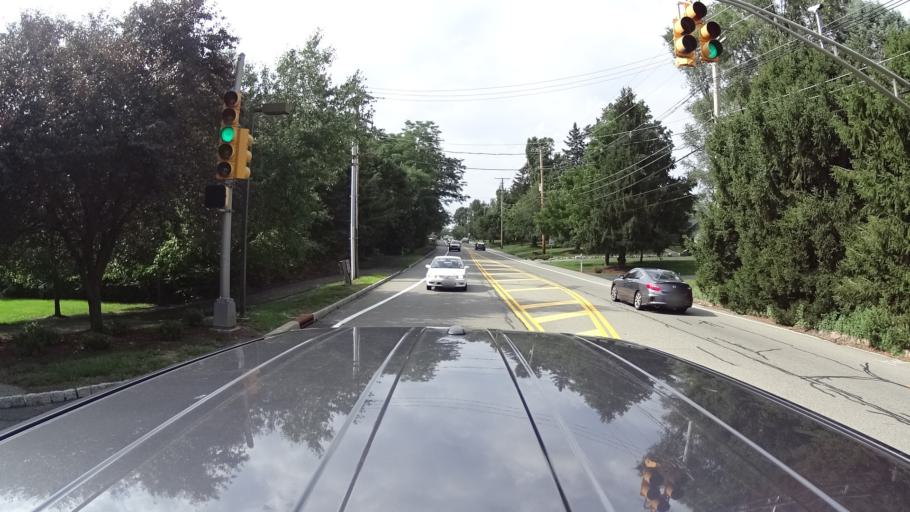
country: US
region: New Jersey
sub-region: Somerset County
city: Warren Township
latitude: 40.6596
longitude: -74.5313
